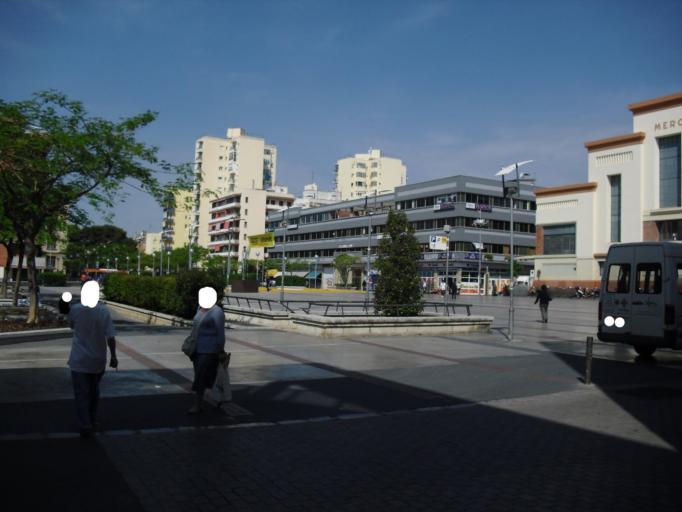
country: ES
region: Catalonia
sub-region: Provincia de Barcelona
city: Vilanova i la Geltru
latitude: 41.2226
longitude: 1.7247
